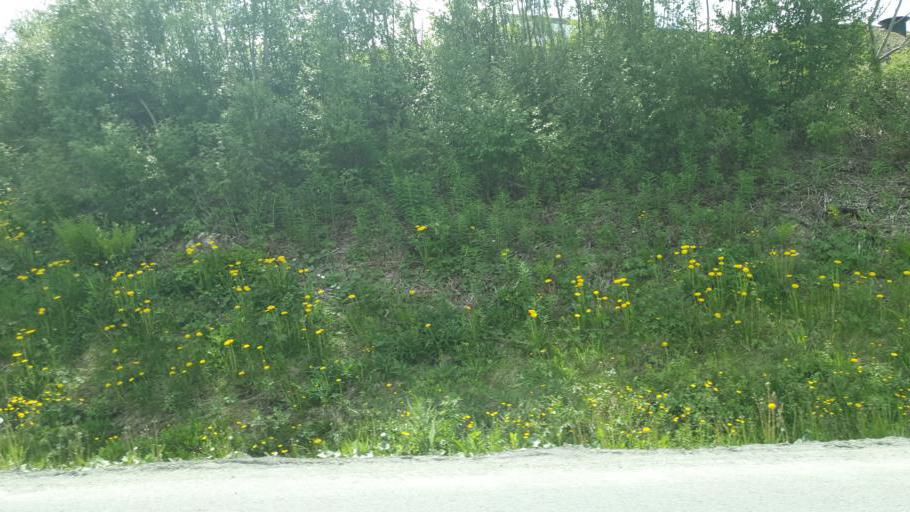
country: NO
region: Nord-Trondelag
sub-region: Leksvik
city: Leksvik
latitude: 63.6837
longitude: 10.5913
